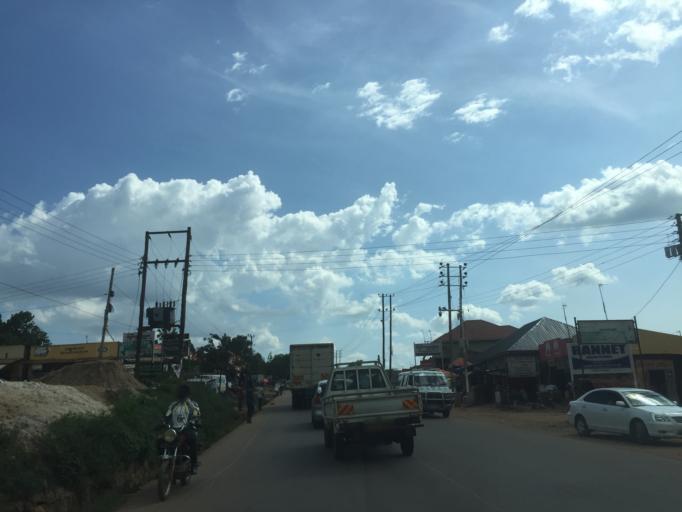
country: UG
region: Central Region
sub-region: Wakiso District
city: Wakiso
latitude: 0.5094
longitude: 32.5252
